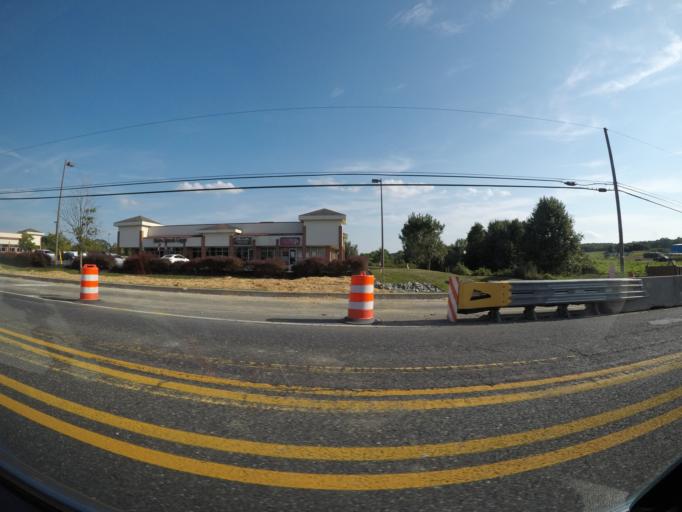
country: US
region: Maryland
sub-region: Harford County
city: South Bel Air
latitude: 39.5549
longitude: -76.2812
